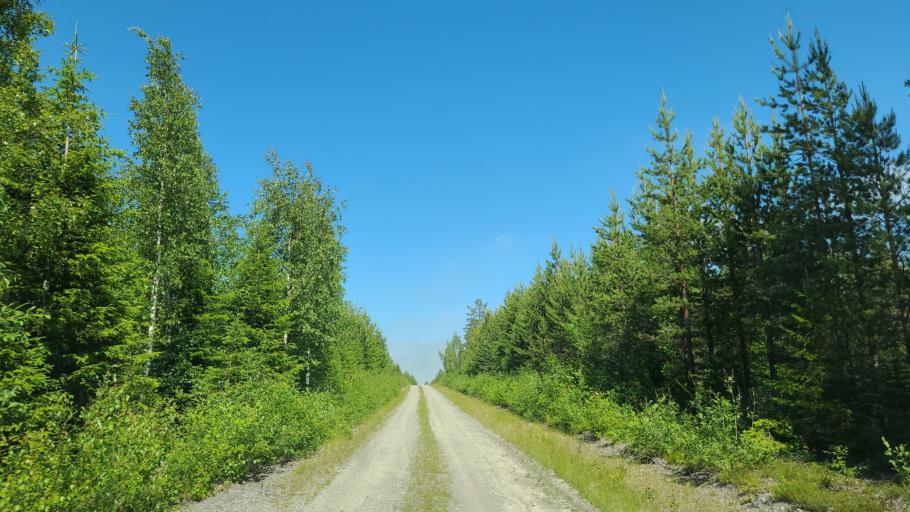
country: SE
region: Vaesternorrland
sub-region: OErnskoeldsviks Kommun
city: Husum
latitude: 63.4374
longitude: 19.2321
